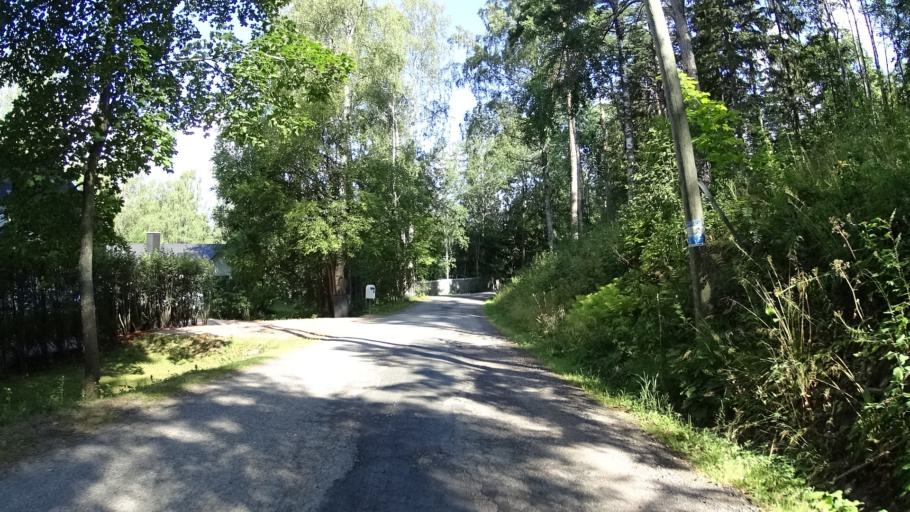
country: FI
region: Uusimaa
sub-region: Helsinki
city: Espoo
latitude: 60.1813
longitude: 24.5914
